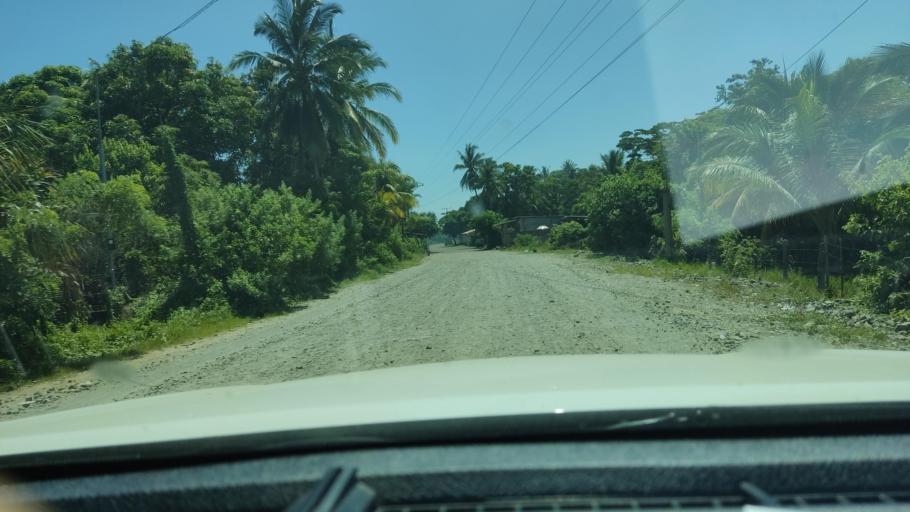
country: SV
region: Ahuachapan
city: San Francisco Menendez
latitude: 13.7646
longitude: -90.1570
